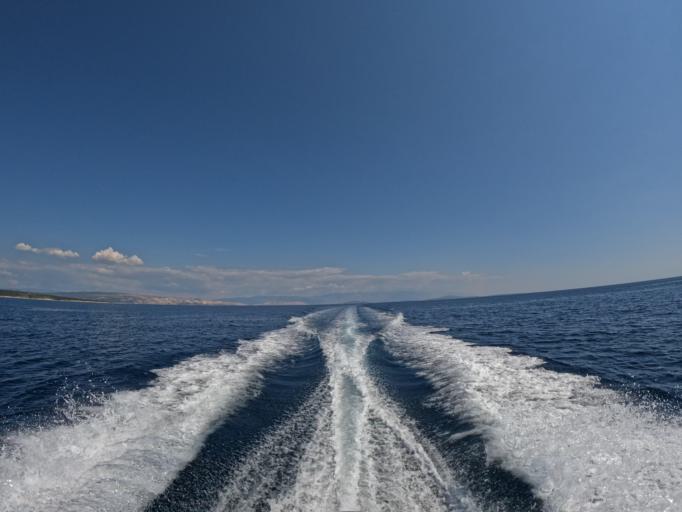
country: HR
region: Primorsko-Goranska
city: Cres
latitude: 44.9395
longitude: 14.4945
